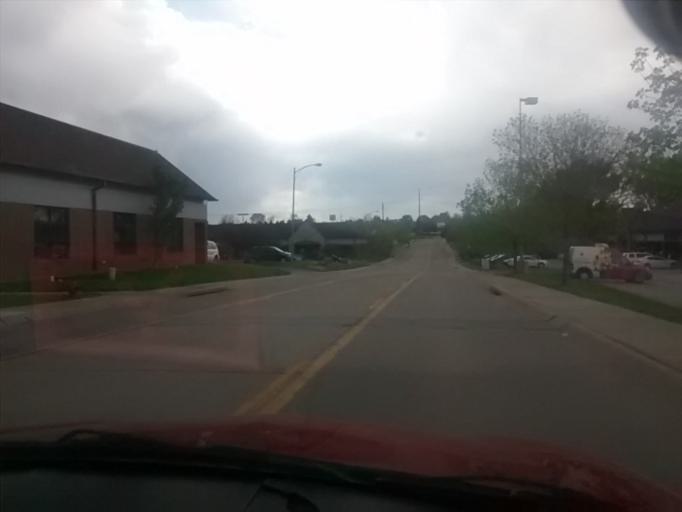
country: US
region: Nebraska
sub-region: Sarpy County
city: Offutt Air Force Base
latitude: 41.1410
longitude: -95.9707
